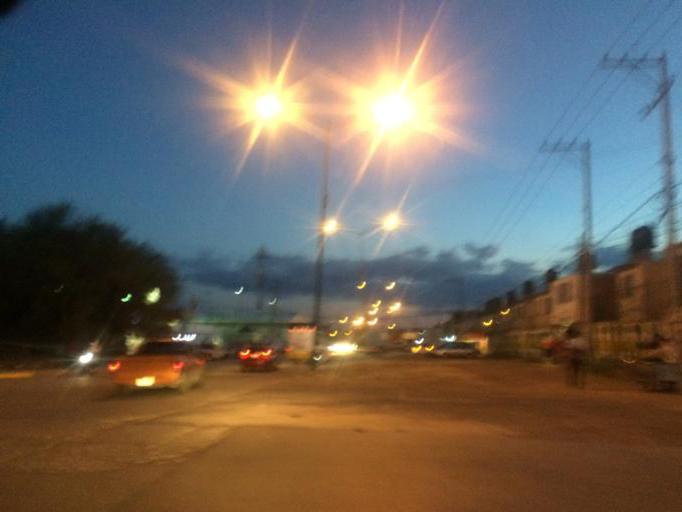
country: MX
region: Guanajuato
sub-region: Leon
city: San Jose de Duran (Los Troncoso)
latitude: 21.0787
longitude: -101.6287
